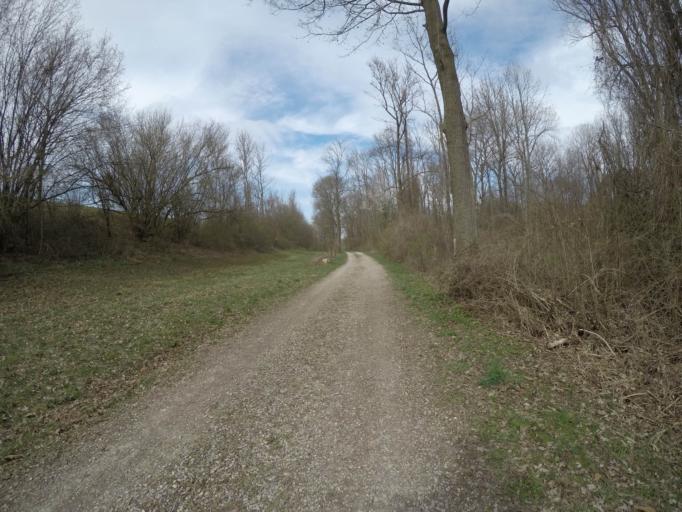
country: DE
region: Bavaria
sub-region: Lower Bavaria
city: Stallwang
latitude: 48.5795
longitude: 12.2190
